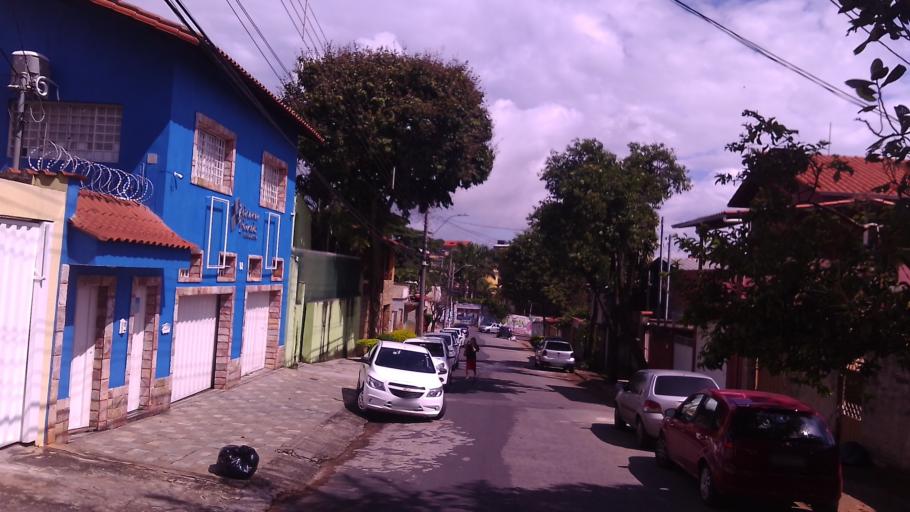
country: BR
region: Minas Gerais
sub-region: Contagem
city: Contagem
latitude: -19.9110
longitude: -44.0193
